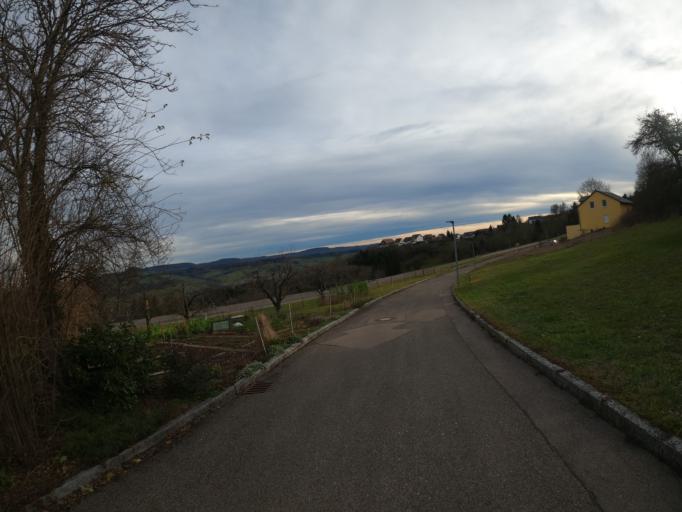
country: DE
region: Baden-Wuerttemberg
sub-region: Regierungsbezirk Stuttgart
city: Ottenbach
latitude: 48.7455
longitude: 9.7222
